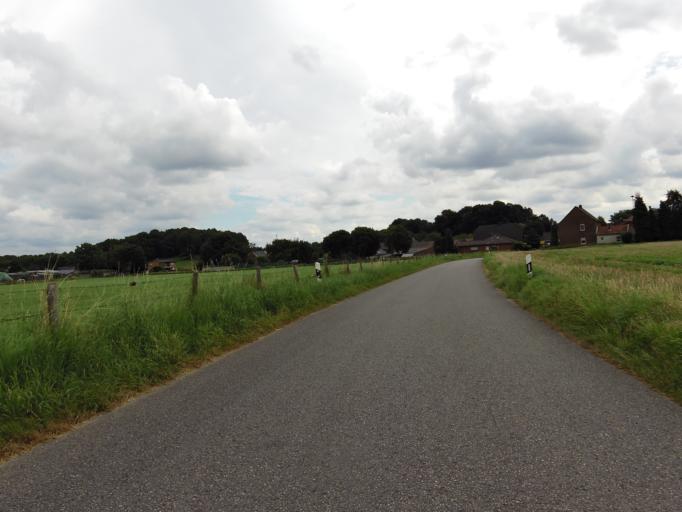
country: DE
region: North Rhine-Westphalia
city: Geilenkirchen
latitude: 50.9702
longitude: 6.0736
